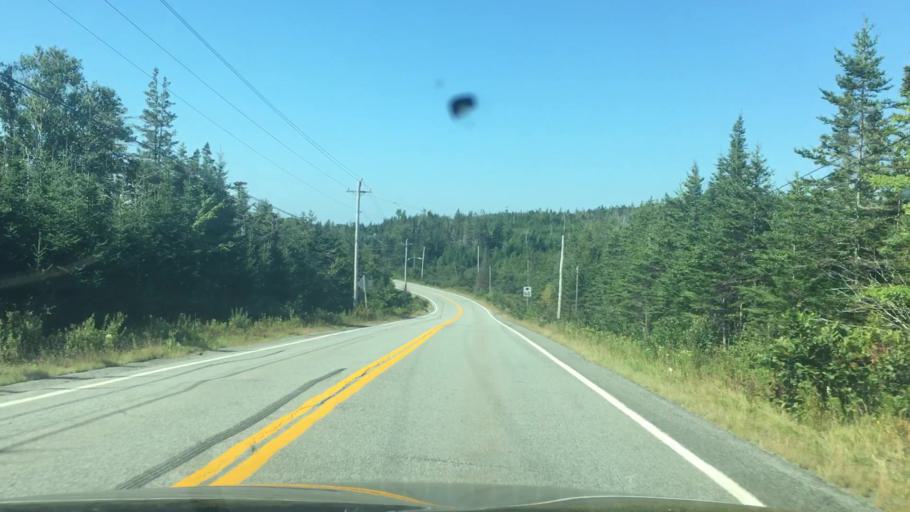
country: CA
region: Nova Scotia
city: New Glasgow
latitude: 44.8083
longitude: -62.6886
